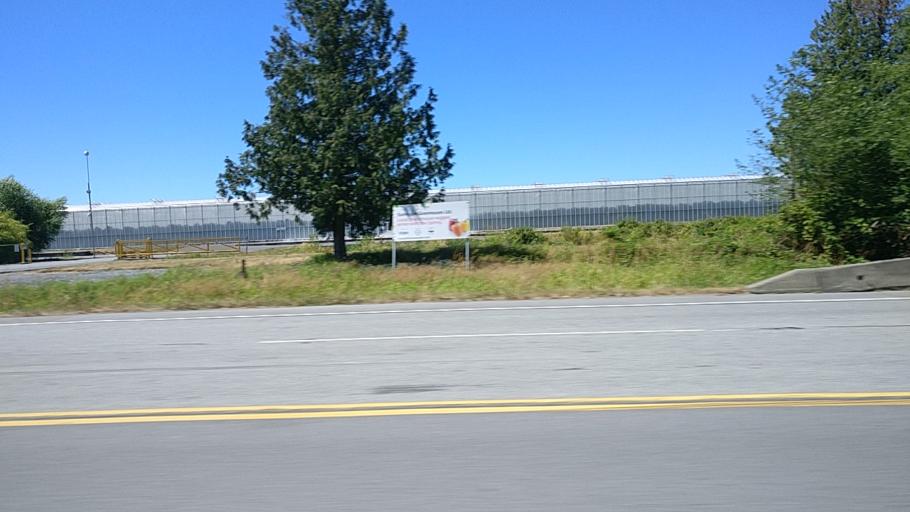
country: US
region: Washington
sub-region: Whatcom County
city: Blaine
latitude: 49.0232
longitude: -122.7352
